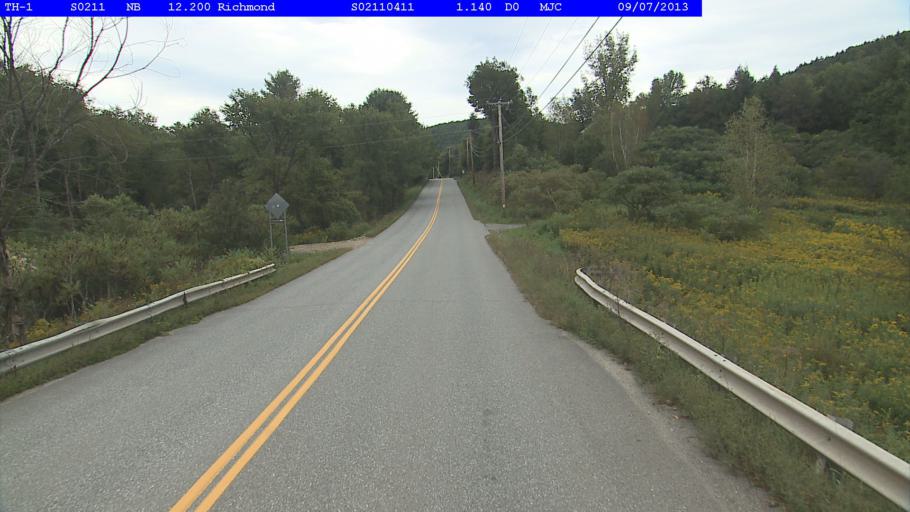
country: US
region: Vermont
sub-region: Chittenden County
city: Williston
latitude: 44.3680
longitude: -72.9996
